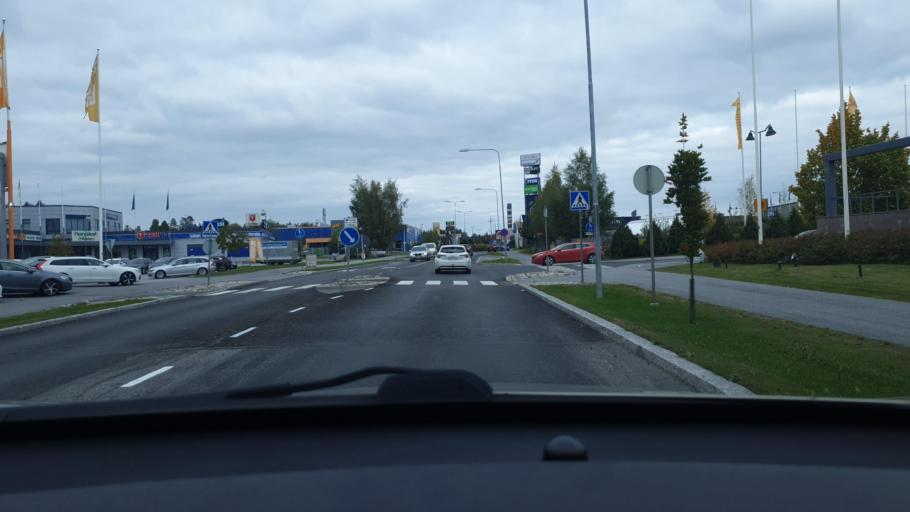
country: FI
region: Ostrobothnia
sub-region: Vaasa
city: Korsholm
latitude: 63.1093
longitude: 21.6499
